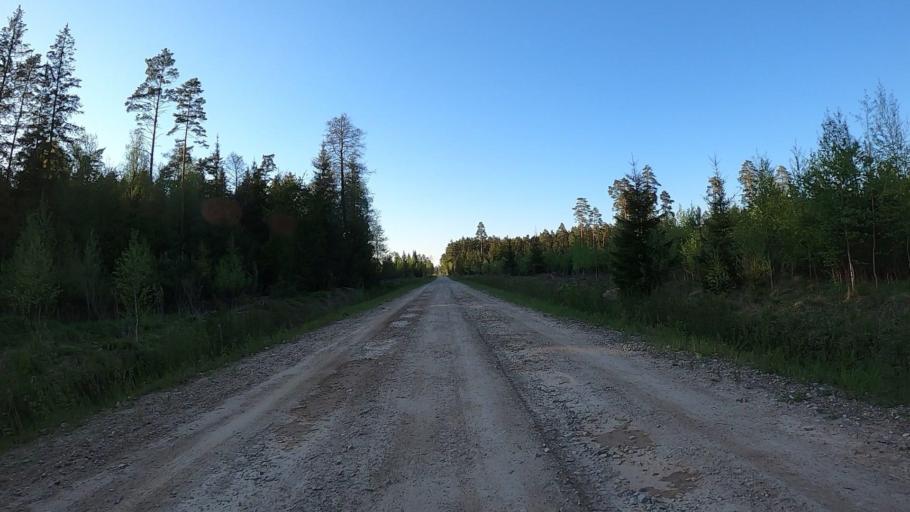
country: LV
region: Kekava
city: Kekava
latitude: 56.7638
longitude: 24.2227
